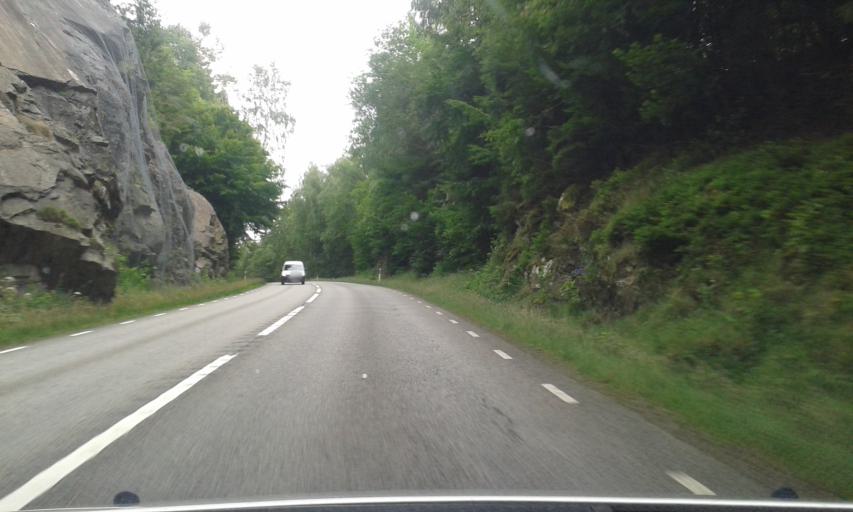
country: SE
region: Halland
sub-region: Varbergs Kommun
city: Tvaaker
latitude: 57.1488
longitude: 12.5968
